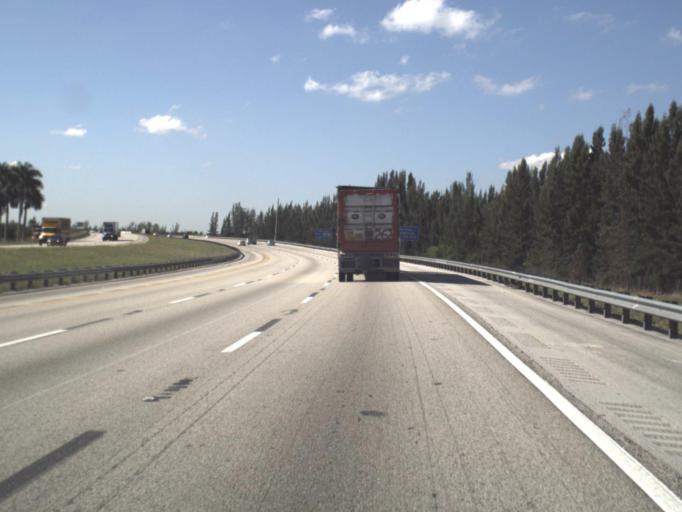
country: US
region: Florida
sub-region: Miami-Dade County
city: Palm Springs North
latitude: 25.9311
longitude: -80.3730
